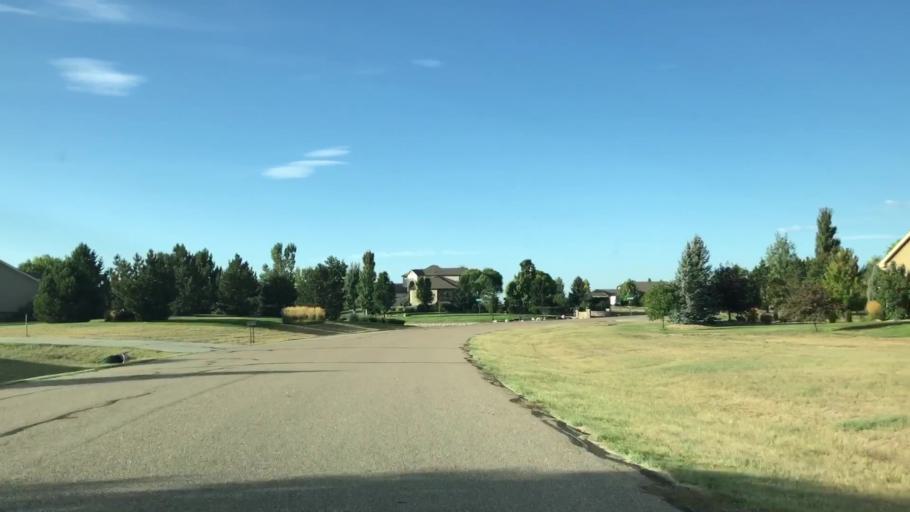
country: US
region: Colorado
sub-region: Weld County
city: Windsor
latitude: 40.4391
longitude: -104.9465
